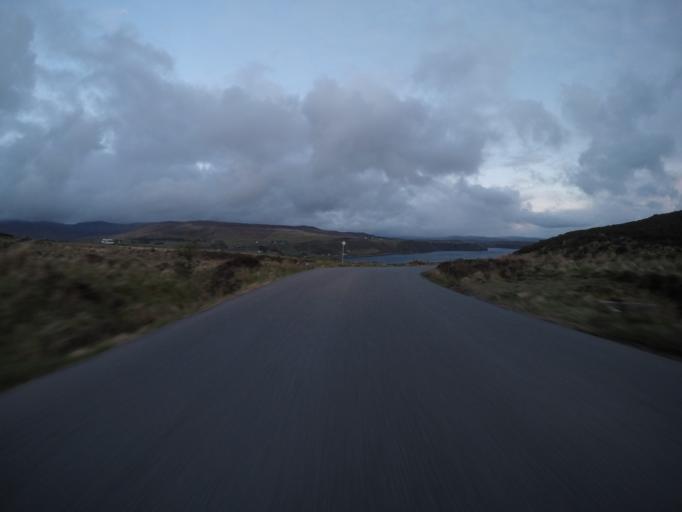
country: GB
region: Scotland
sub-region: Highland
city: Portree
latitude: 57.5942
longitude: -6.3733
